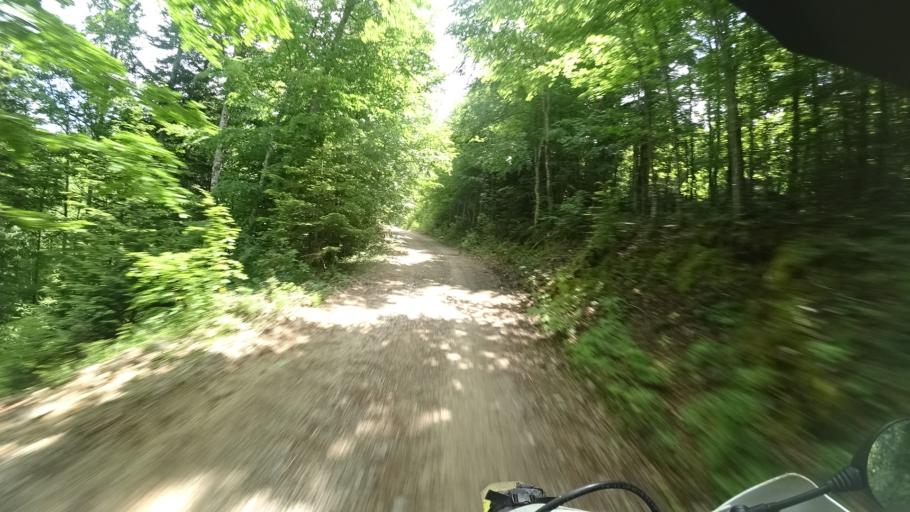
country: HR
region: Zadarska
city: Gracac
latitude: 44.4880
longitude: 15.8731
